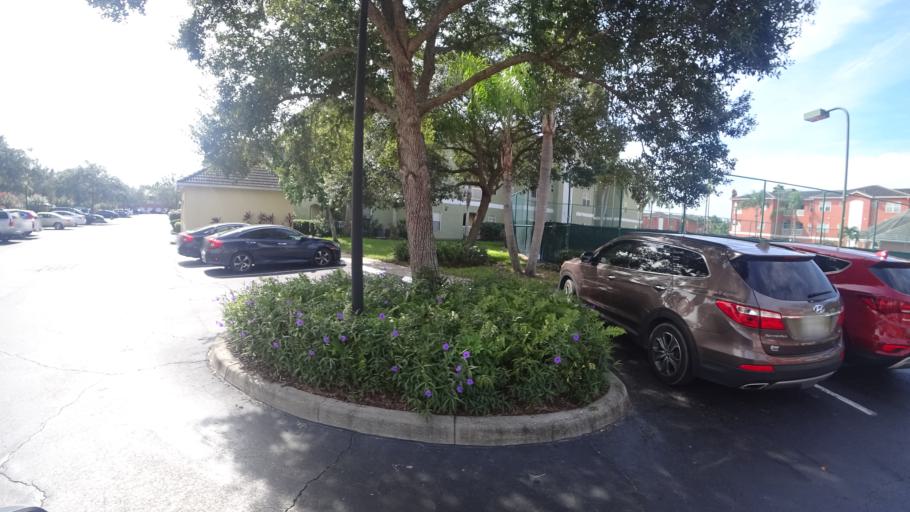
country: US
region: Florida
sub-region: Sarasota County
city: The Meadows
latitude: 27.3872
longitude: -82.4690
